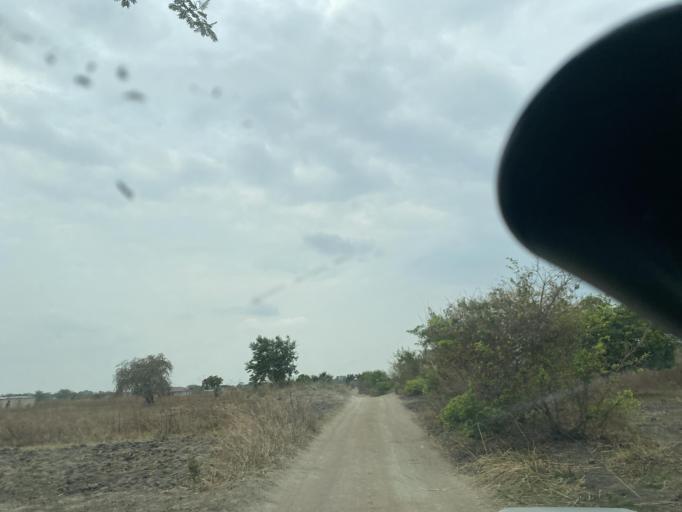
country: ZM
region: Lusaka
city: Lusaka
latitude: -15.2391
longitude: 28.3338
